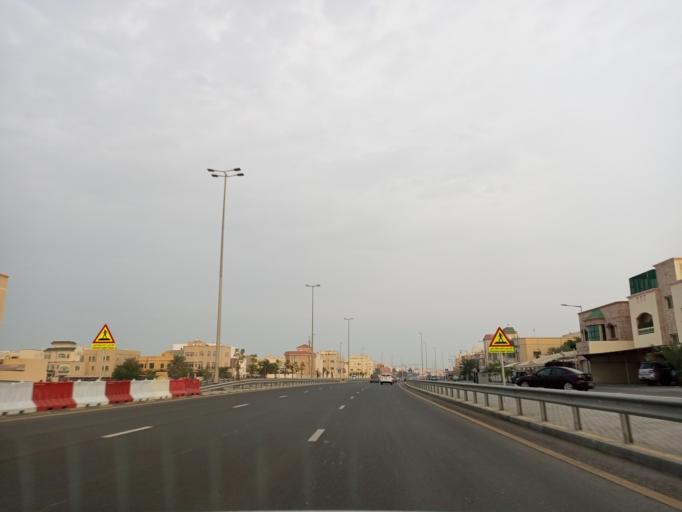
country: BH
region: Muharraq
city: Al Hadd
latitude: 26.2473
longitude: 50.6445
